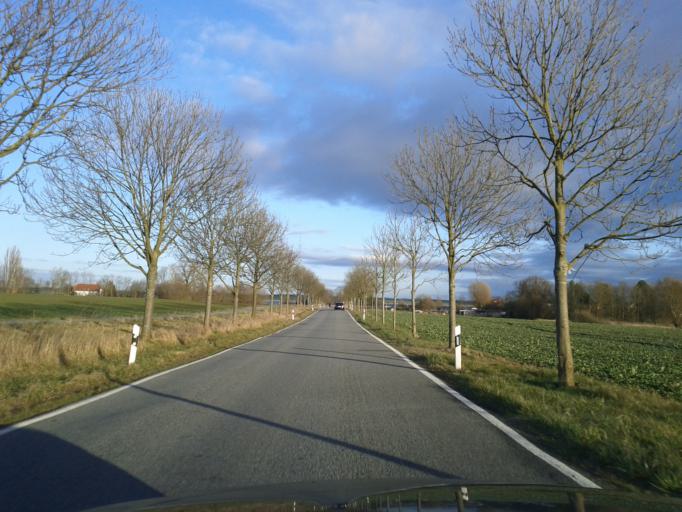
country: DE
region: Mecklenburg-Vorpommern
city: Wismar
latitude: 53.9870
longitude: 11.4191
